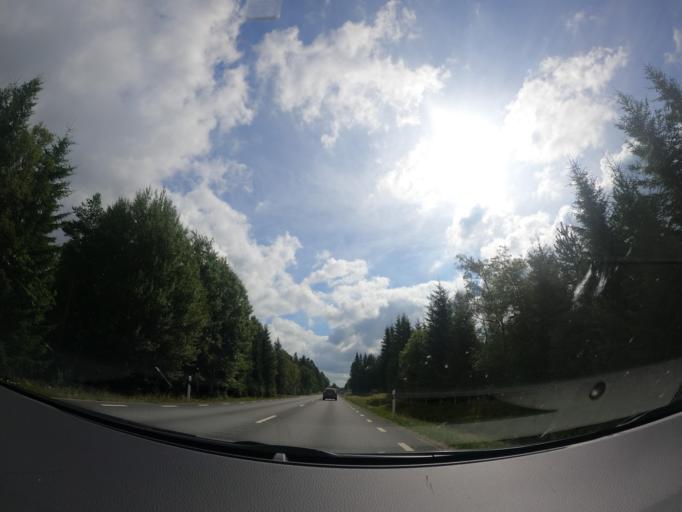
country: SE
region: Joenkoeping
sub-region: Gislaveds Kommun
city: Smalandsstenar
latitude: 57.1215
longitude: 13.3664
